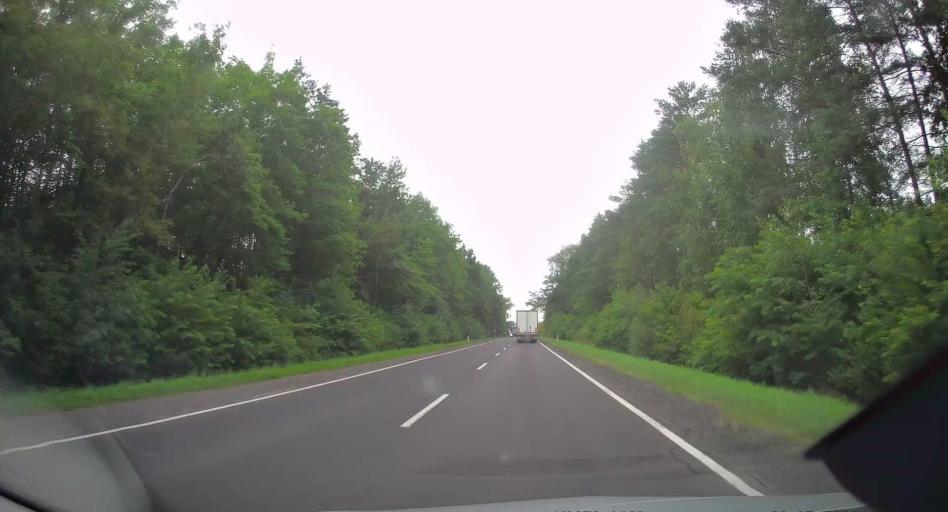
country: PL
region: Lodz Voivodeship
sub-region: Powiat radomszczanski
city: Radomsko
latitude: 51.0385
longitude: 19.4368
